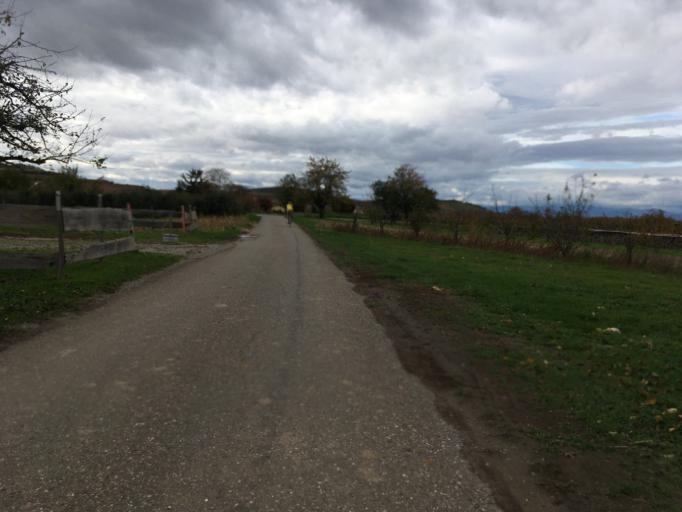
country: DE
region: Baden-Wuerttemberg
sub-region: Freiburg Region
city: Wyhl
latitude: 48.1373
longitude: 7.6546
